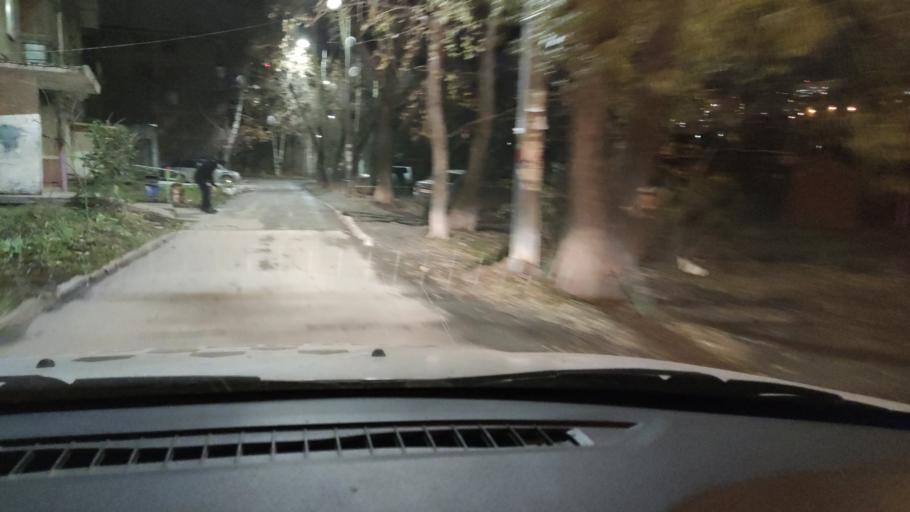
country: RU
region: Perm
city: Perm
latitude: 57.9933
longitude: 56.2330
